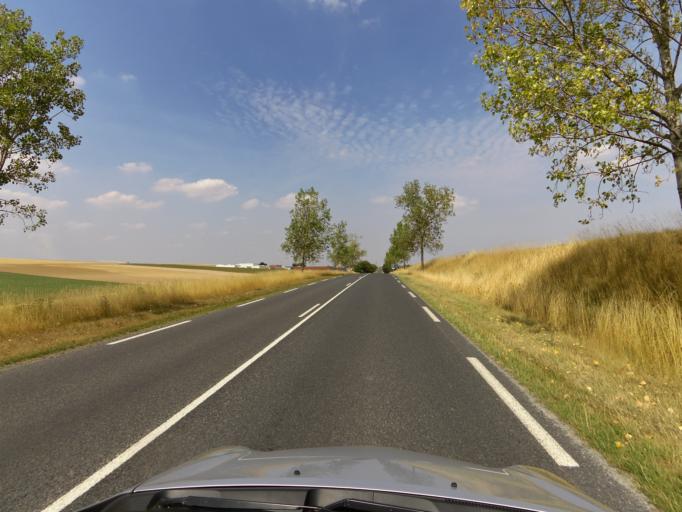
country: FR
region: Champagne-Ardenne
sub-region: Departement de la Marne
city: Rilly-la-Montagne
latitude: 49.1876
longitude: 4.0128
